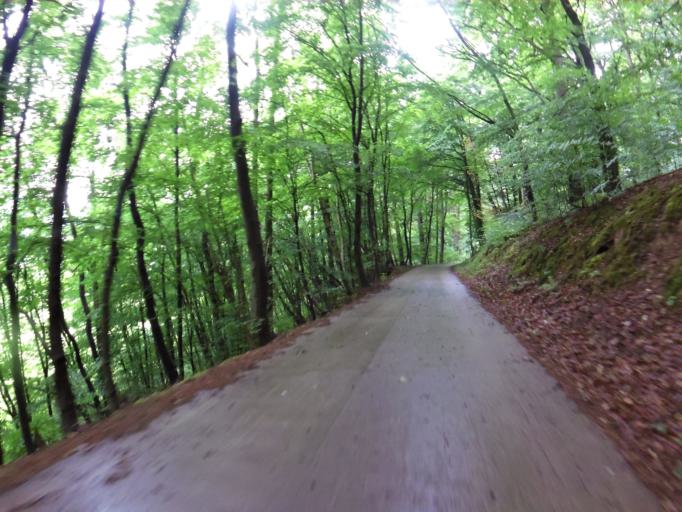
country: DE
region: Hesse
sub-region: Regierungsbezirk Kassel
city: Bad Hersfeld
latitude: 50.8802
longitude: 9.7281
